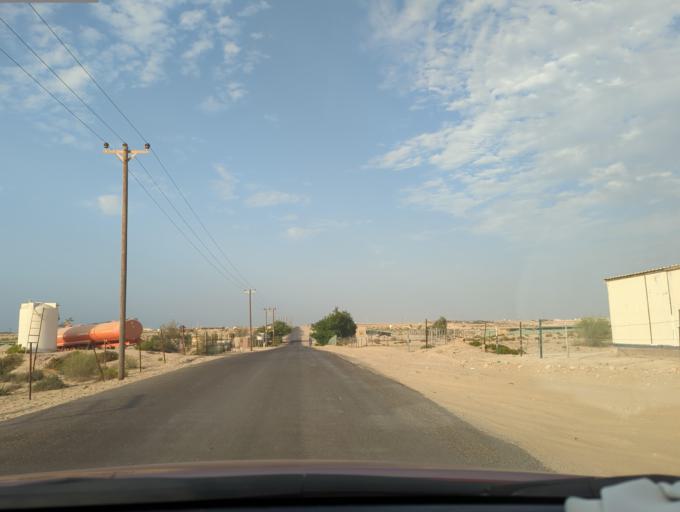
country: AE
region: Dubai
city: Dubai
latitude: 24.7152
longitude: 54.8689
